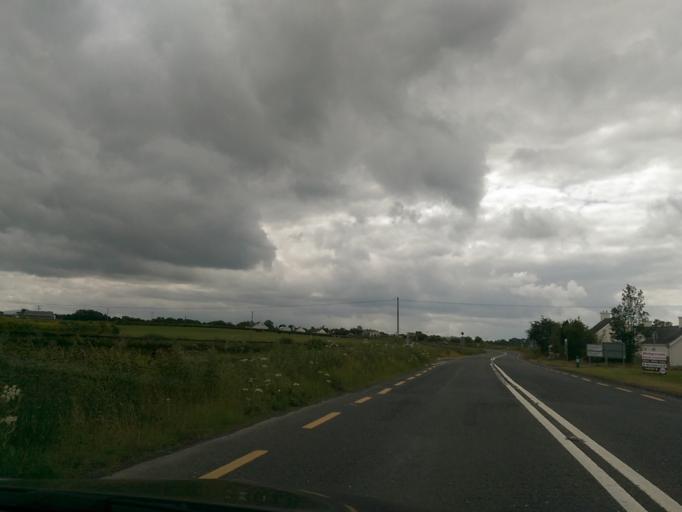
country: IE
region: Munster
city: Thurles
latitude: 52.6328
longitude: -7.7790
